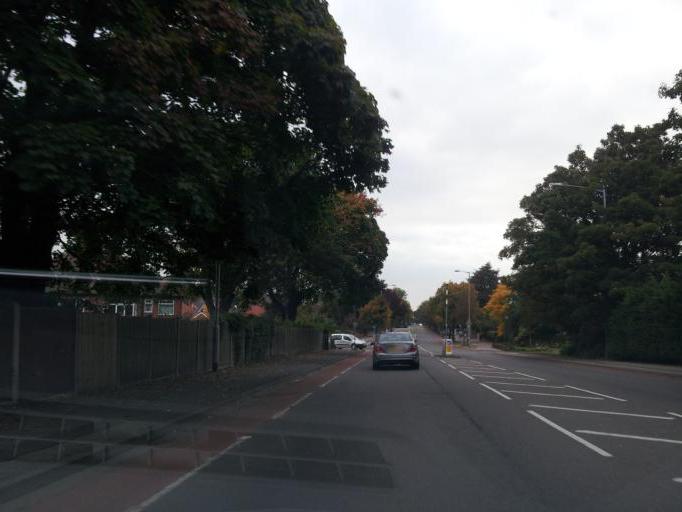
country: GB
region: England
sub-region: Nottinghamshire
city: Newark on Trent
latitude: 53.0669
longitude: -0.7945
